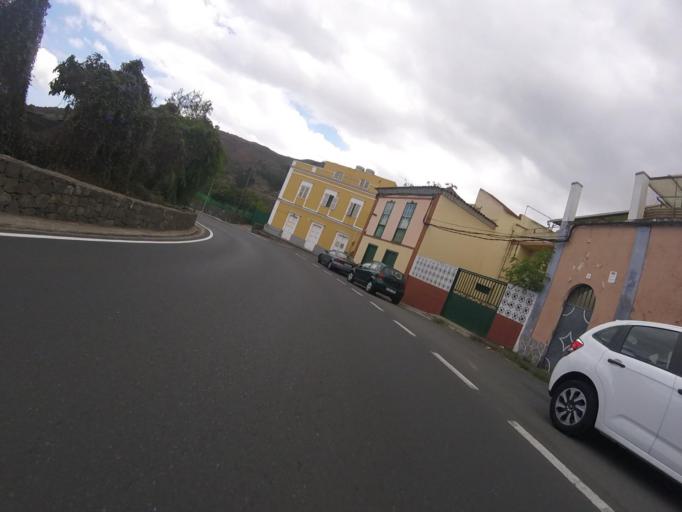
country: ES
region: Canary Islands
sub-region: Provincia de Las Palmas
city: Santa Brigida
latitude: 28.0252
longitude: -15.5044
